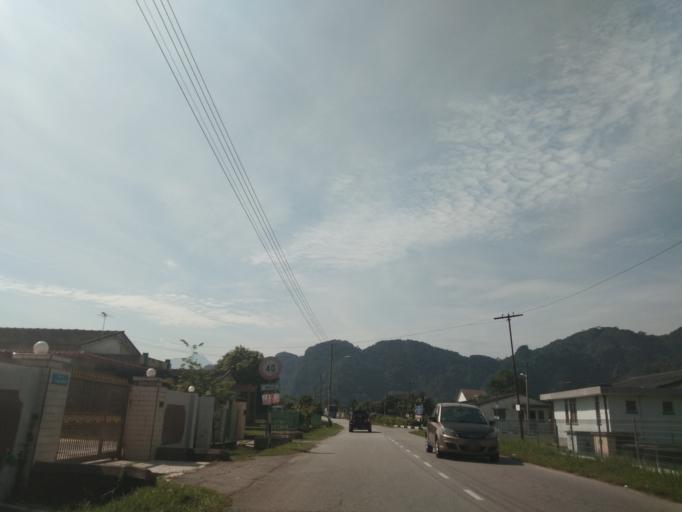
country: MY
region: Perak
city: Ipoh
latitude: 4.5701
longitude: 101.1252
